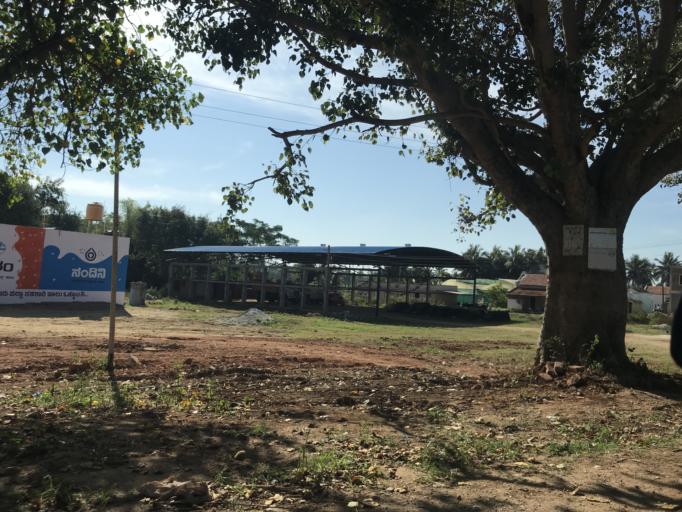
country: IN
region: Karnataka
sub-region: Mysore
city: Mysore
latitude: 12.2125
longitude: 76.5617
